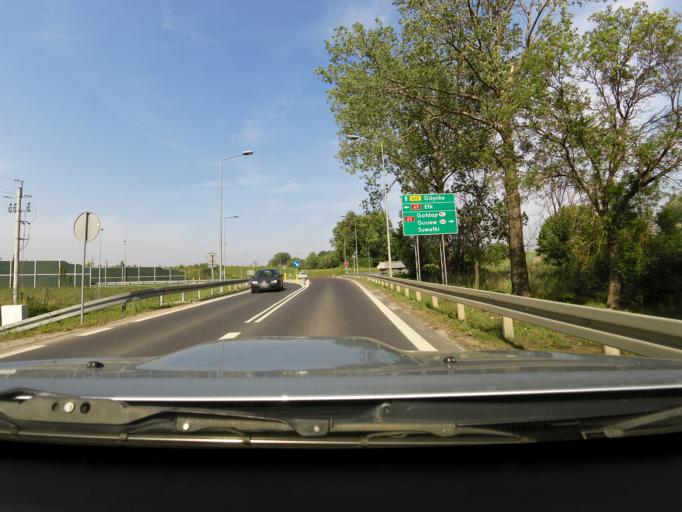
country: PL
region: Warmian-Masurian Voivodeship
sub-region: Powiat olecki
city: Olecko
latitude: 54.0428
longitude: 22.4719
